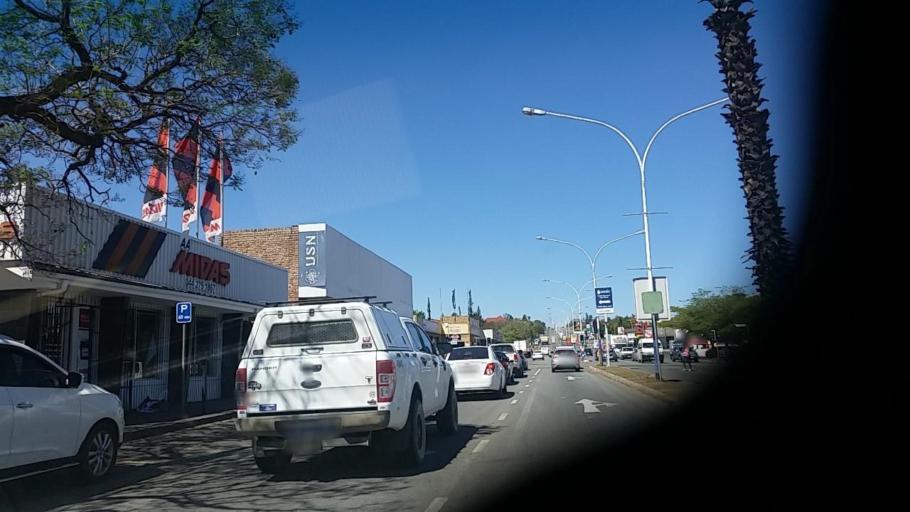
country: ZA
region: Western Cape
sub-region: Eden District Municipality
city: Oudtshoorn
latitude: -33.5929
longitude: 22.2040
